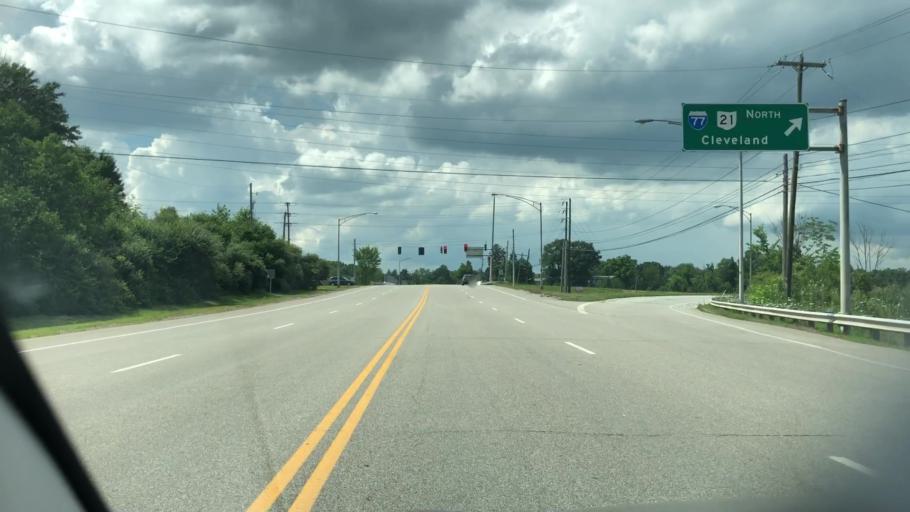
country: US
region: Ohio
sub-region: Summit County
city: Montrose-Ghent
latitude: 41.1492
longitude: -81.6284
